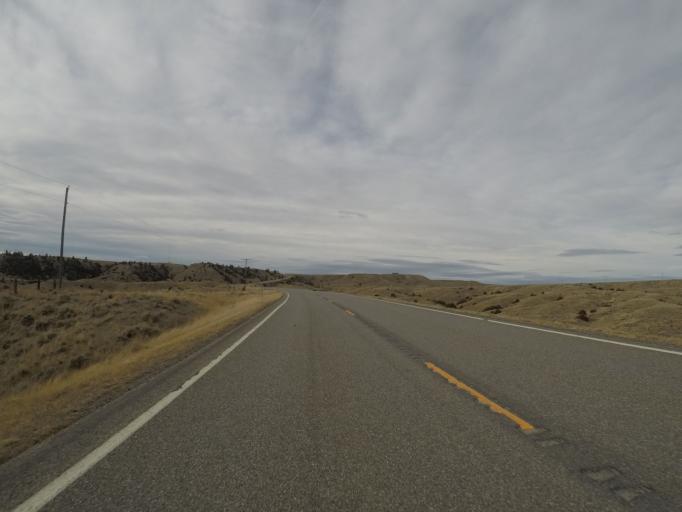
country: US
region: Montana
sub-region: Yellowstone County
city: Laurel
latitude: 45.8516
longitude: -108.7500
